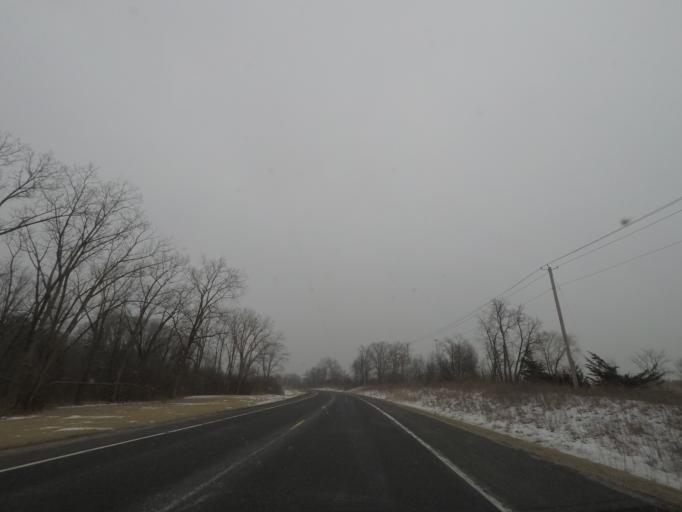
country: US
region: New York
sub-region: Albany County
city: Delmar
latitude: 42.5681
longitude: -73.8518
